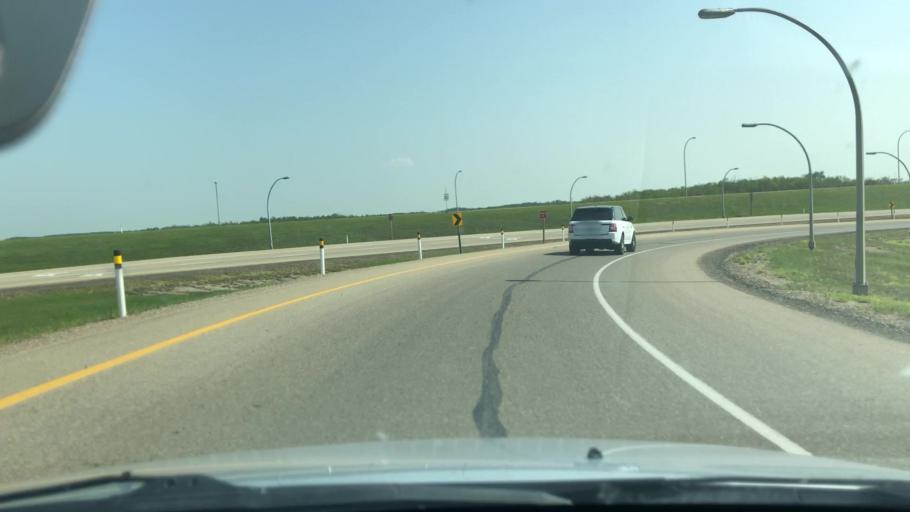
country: CA
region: Alberta
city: Edmonton
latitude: 53.6484
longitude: -113.4905
